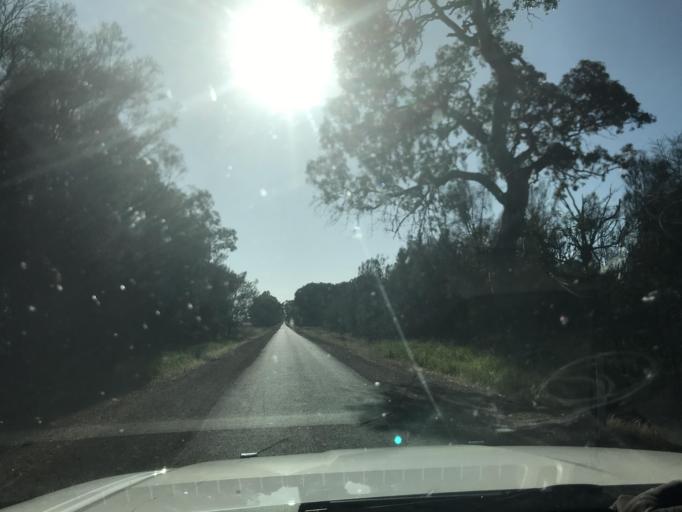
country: AU
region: Victoria
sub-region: Horsham
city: Horsham
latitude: -37.0053
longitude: 141.6231
